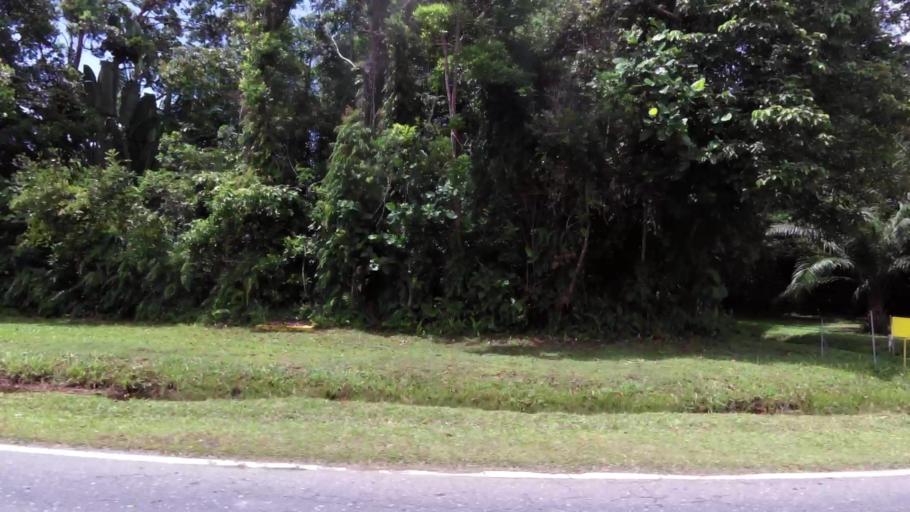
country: BN
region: Belait
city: Kuala Belait
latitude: 4.5993
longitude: 114.2696
